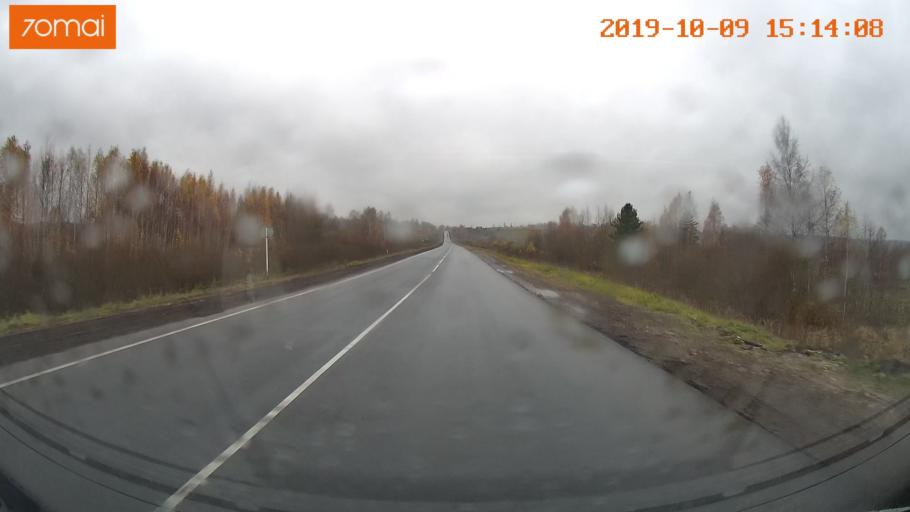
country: RU
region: Kostroma
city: Susanino
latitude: 58.1381
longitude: 41.6056
